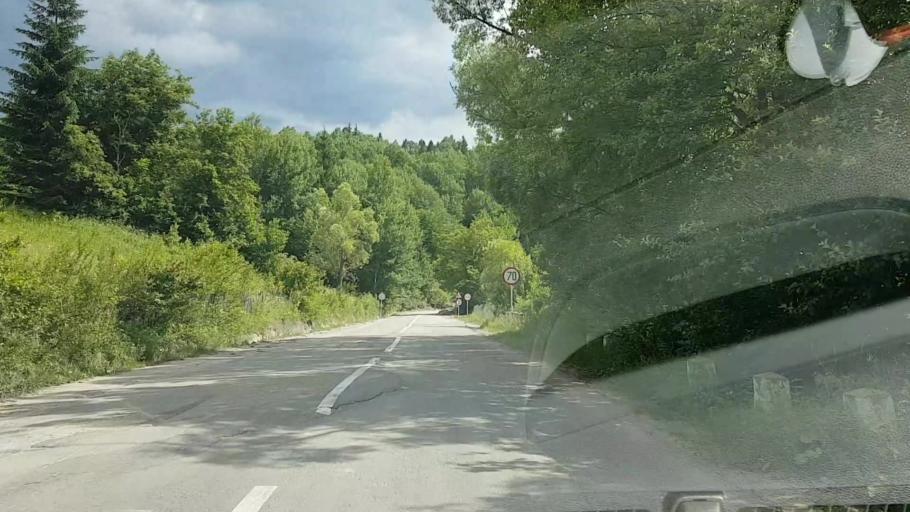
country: RO
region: Neamt
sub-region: Comuna Poiana Teiului
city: Poiana Teiului
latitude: 47.0807
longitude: 25.9678
